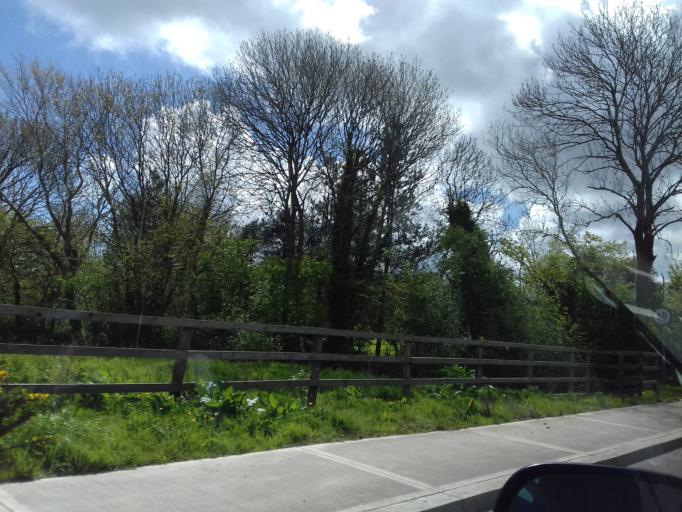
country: IE
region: Leinster
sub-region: Loch Garman
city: Loch Garman
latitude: 52.3577
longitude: -6.4528
